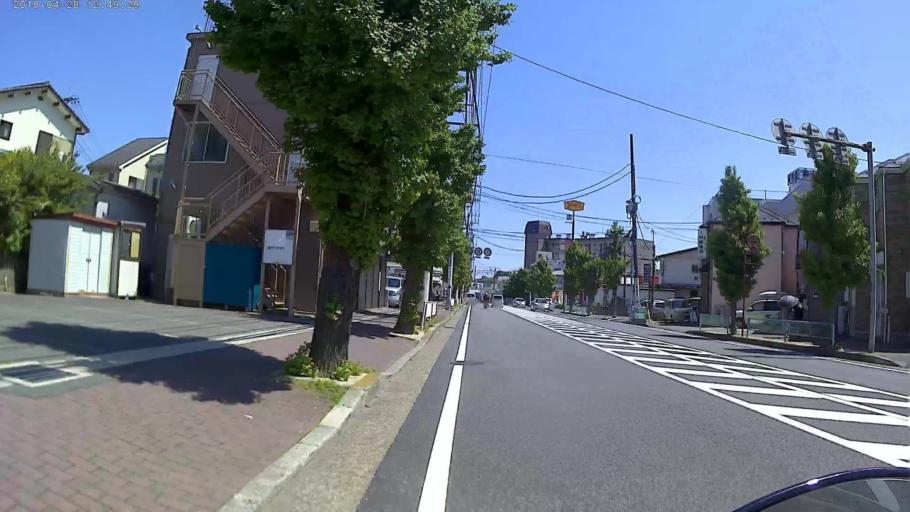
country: JP
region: Kanagawa
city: Yokosuka
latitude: 35.2620
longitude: 139.6531
